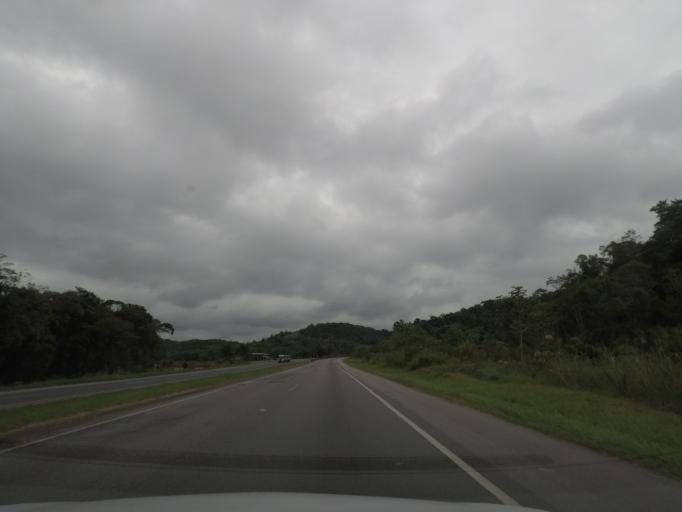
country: BR
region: Sao Paulo
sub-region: Juquia
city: Juquia
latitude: -24.3737
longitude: -47.7073
